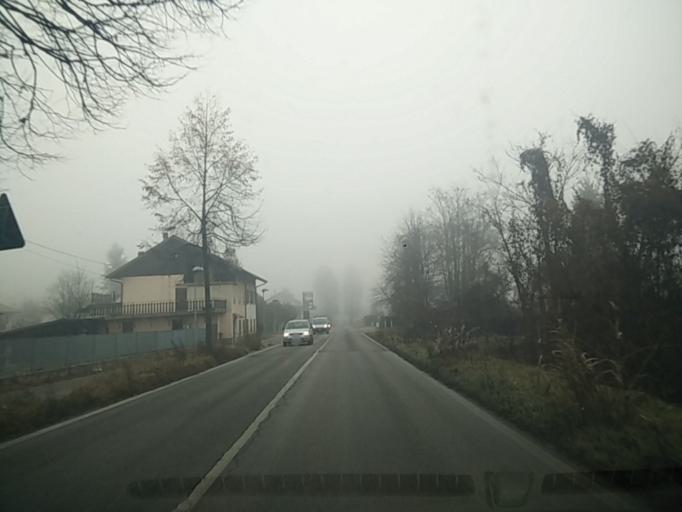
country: IT
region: Veneto
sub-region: Provincia di Belluno
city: Seren del Grappa
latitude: 46.0137
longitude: 11.8728
